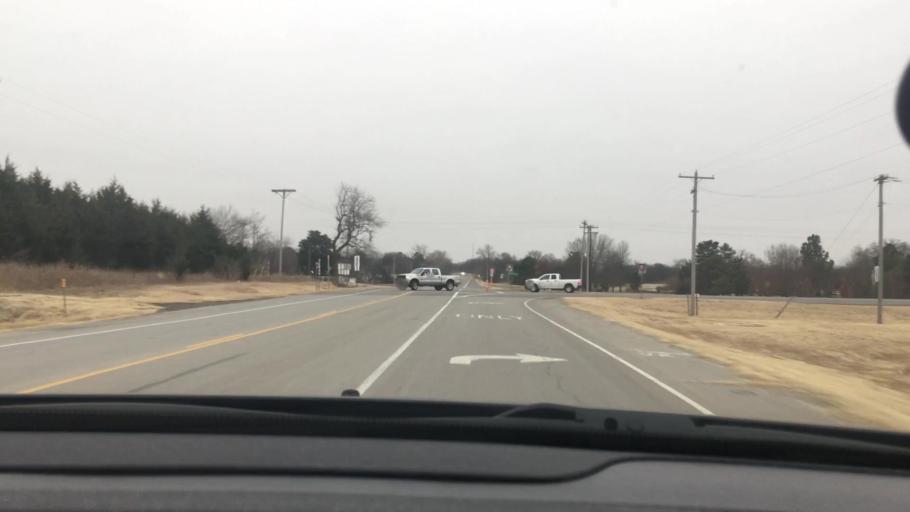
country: US
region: Oklahoma
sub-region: Garvin County
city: Wynnewood
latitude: 34.6238
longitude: -97.1630
